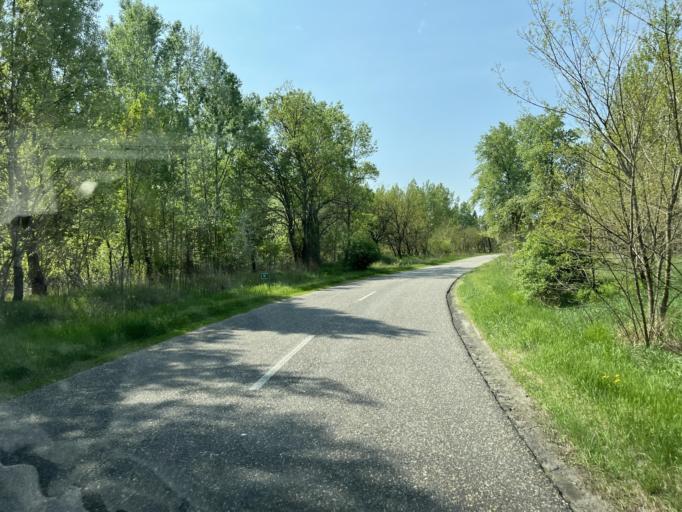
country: HU
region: Pest
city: Kocser
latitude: 47.0643
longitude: 19.8622
